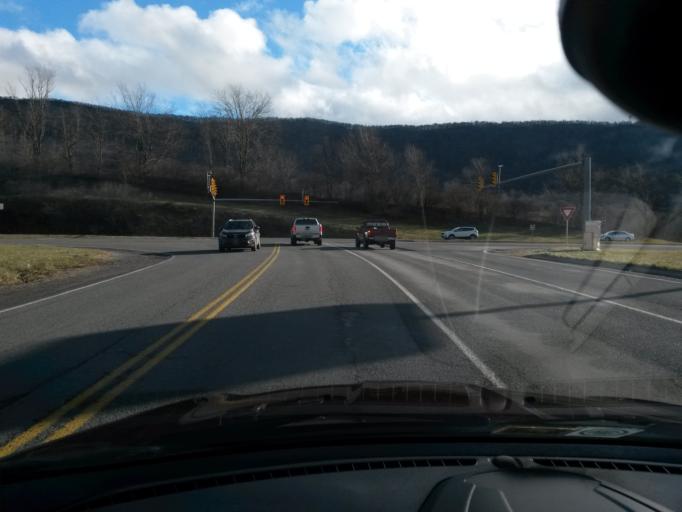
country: US
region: Virginia
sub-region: Tazewell County
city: Bluefield
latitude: 37.2382
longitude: -81.2488
